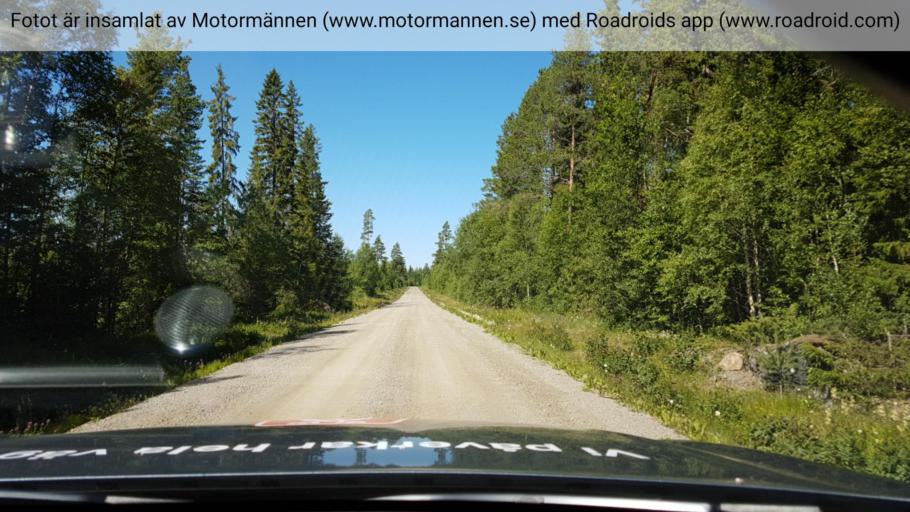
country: SE
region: Jaemtland
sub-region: Braecke Kommun
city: Braecke
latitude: 62.8008
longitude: 15.2412
